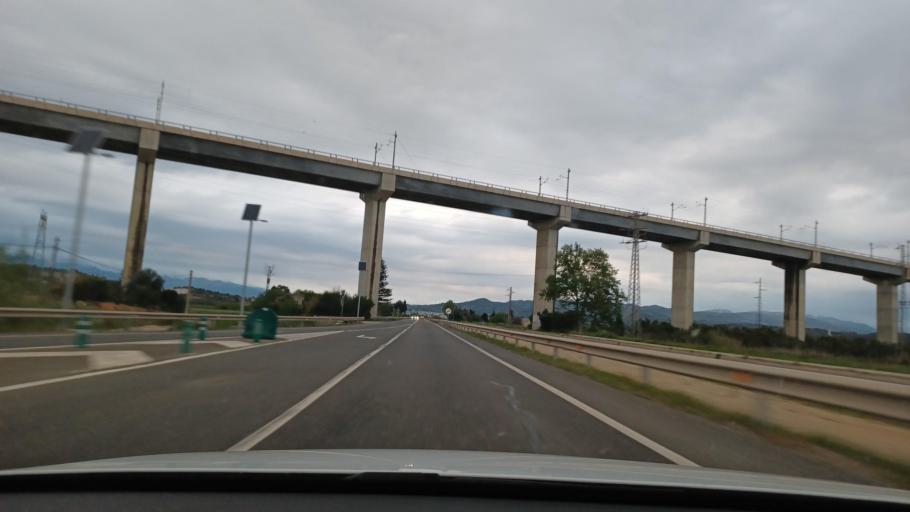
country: ES
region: Catalonia
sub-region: Provincia de Tarragona
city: Amposta
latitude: 40.7276
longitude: 0.5712
